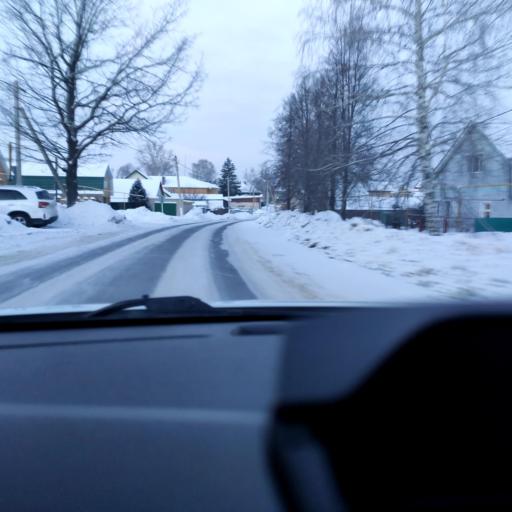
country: RU
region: Tatarstan
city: Vysokaya Gora
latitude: 55.9342
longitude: 49.3117
